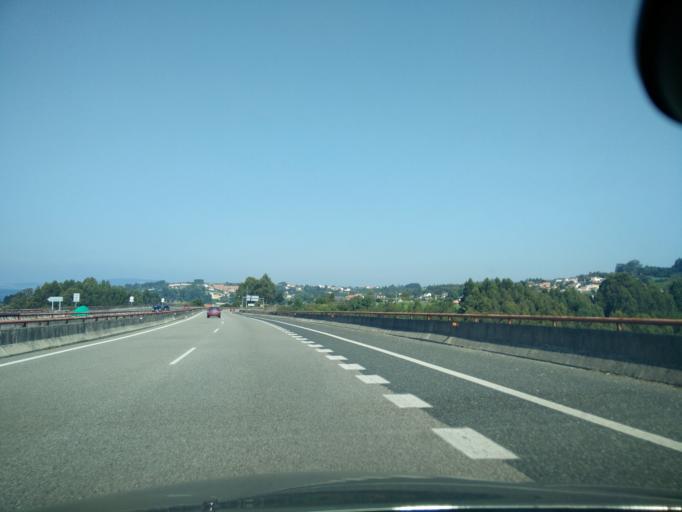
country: ES
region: Galicia
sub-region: Provincia da Coruna
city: Mino
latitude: 43.3518
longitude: -8.2012
